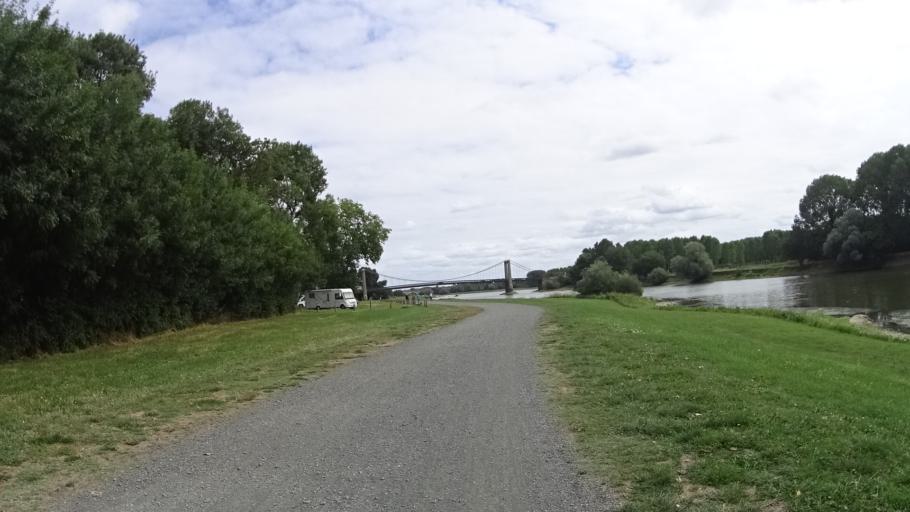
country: FR
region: Pays de la Loire
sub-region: Departement de Maine-et-Loire
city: Bouchemaine
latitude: 47.4176
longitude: -0.6118
